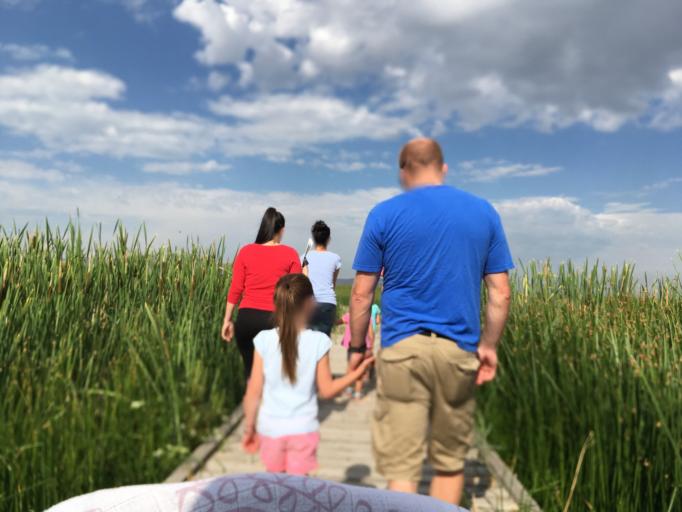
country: US
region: Utah
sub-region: Davis County
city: Layton
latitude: 41.0370
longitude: -112.0244
